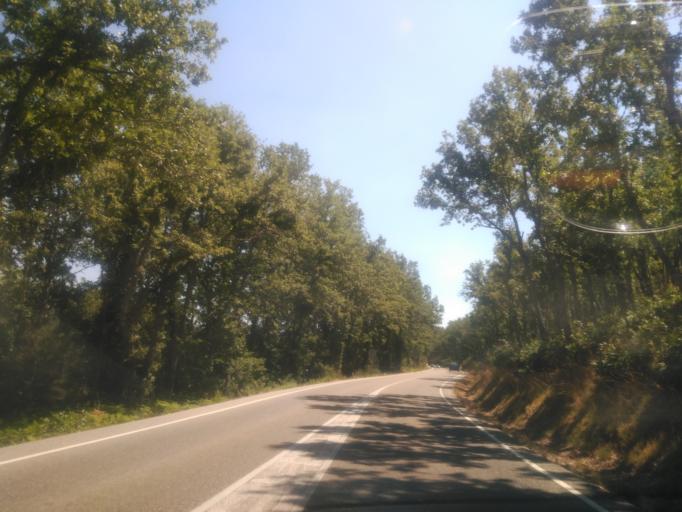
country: ES
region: Castille and Leon
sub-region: Provincia de Zamora
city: Galende
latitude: 42.1190
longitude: -6.6975
